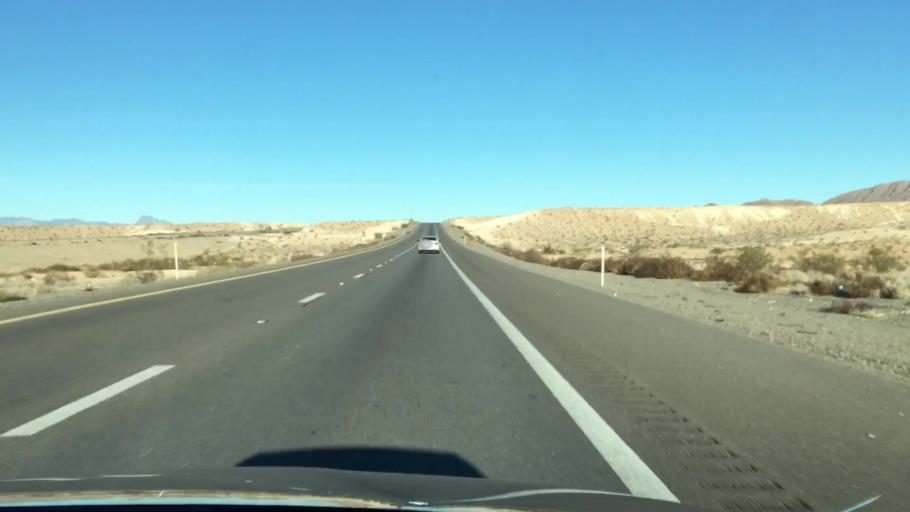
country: US
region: Nevada
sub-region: Clark County
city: Moapa Town
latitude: 36.5660
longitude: -114.6763
